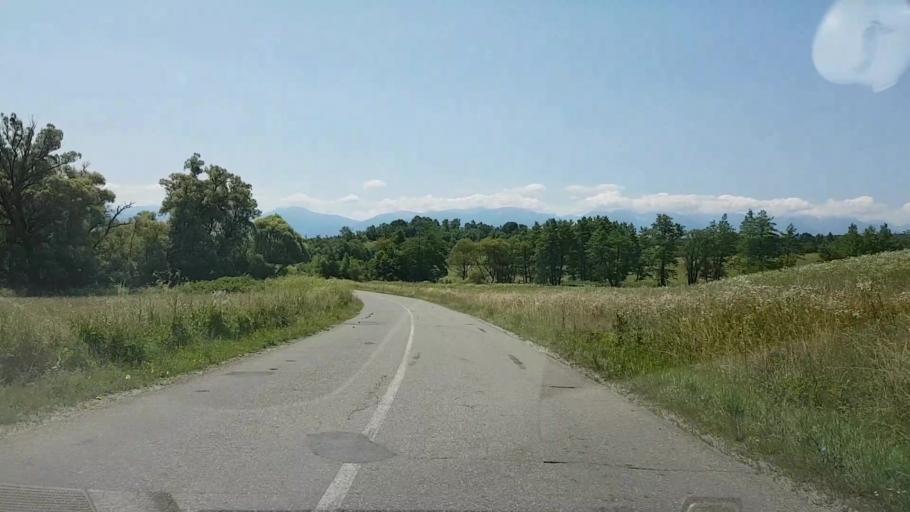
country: RO
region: Brasov
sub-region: Comuna Voila
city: Voila
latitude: 45.8625
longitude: 24.8254
